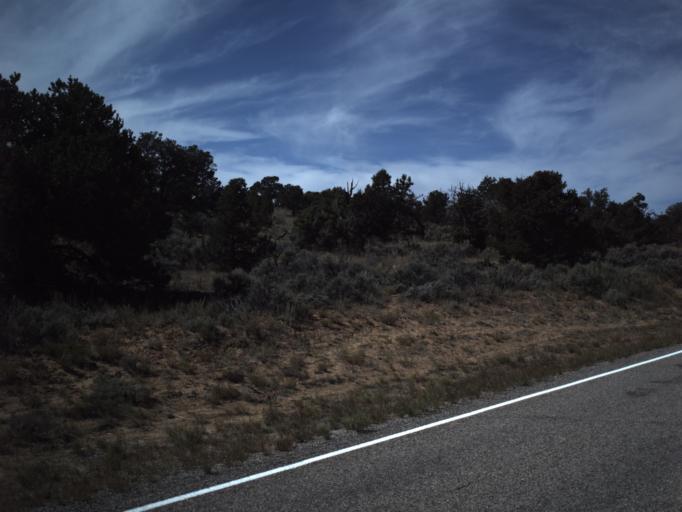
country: US
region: Utah
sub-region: Wayne County
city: Loa
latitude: 37.8725
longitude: -111.4457
